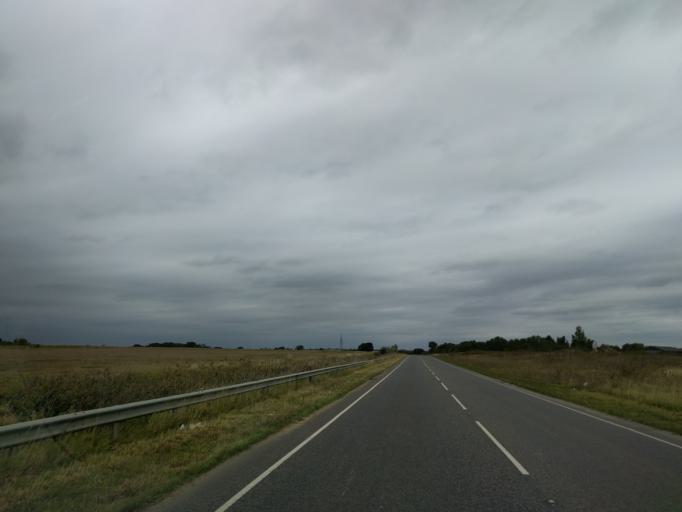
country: GB
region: England
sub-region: Cambridgeshire
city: Swavesey
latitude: 52.2796
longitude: 0.0371
